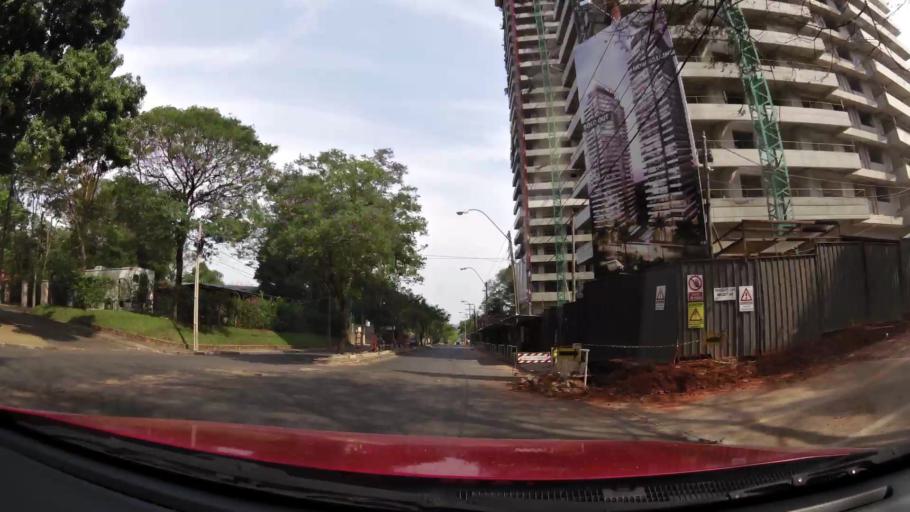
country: PY
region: Asuncion
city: Asuncion
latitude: -25.2628
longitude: -57.5738
